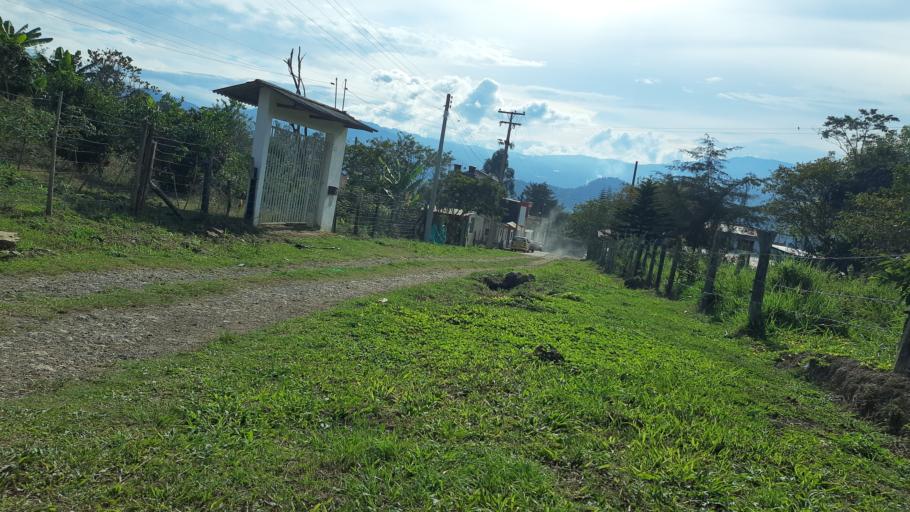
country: CO
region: Boyaca
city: Garagoa
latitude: 5.0908
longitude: -73.3623
